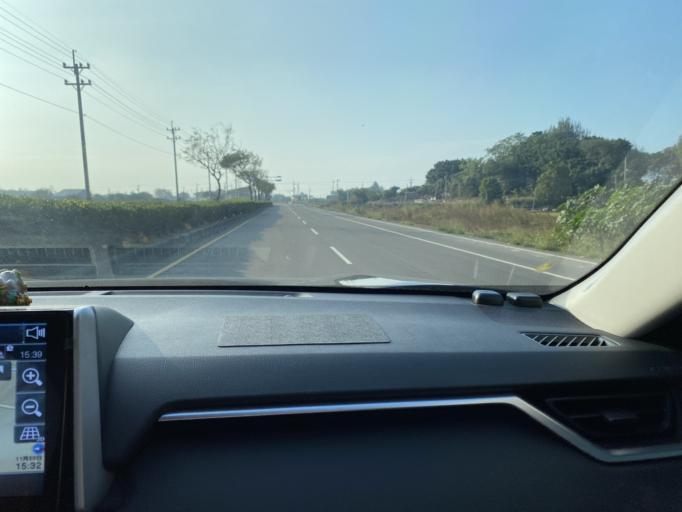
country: TW
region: Taiwan
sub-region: Changhua
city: Chang-hua
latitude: 23.9607
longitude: 120.3928
